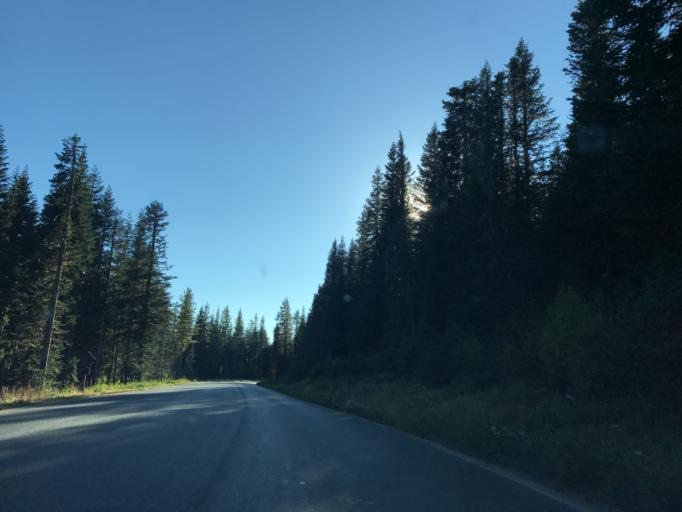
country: US
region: Washington
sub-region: Pierce County
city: Buckley
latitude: 46.7765
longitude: -121.7543
